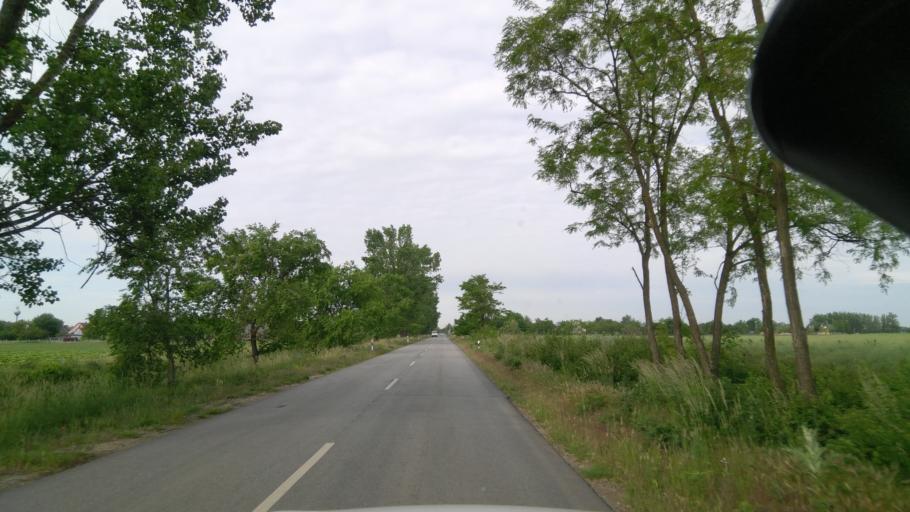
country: HU
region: Bekes
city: Ketegyhaza
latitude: 46.5556
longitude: 21.1936
